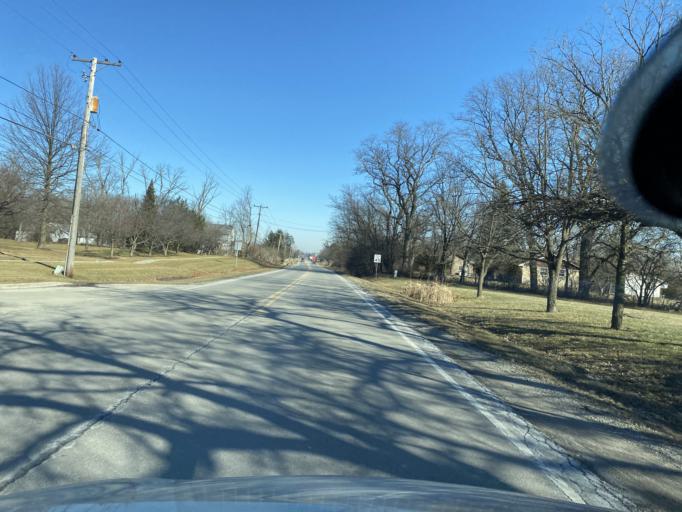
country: US
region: Illinois
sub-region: Cook County
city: Lemont
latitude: 41.6598
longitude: -87.9684
